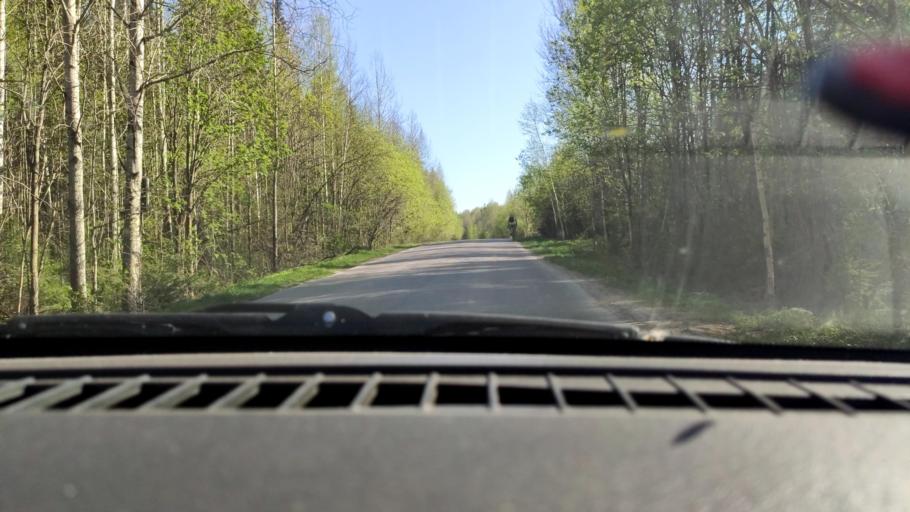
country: RU
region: Perm
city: Overyata
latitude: 58.0741
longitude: 56.0015
